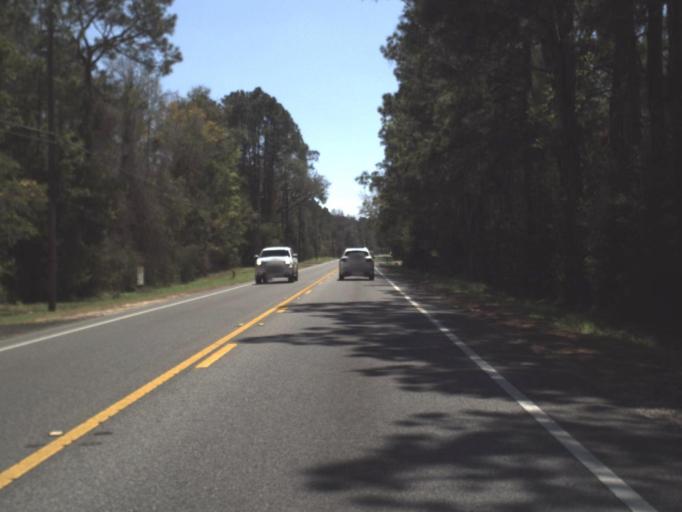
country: US
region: Florida
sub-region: Leon County
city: Woodville
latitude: 30.3378
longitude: -84.2536
